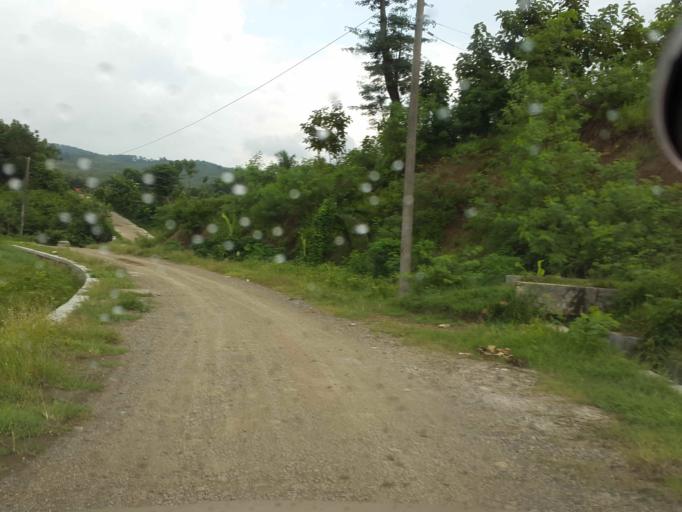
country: ID
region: Central Java
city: Pamedaran
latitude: -7.1068
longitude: 108.9003
